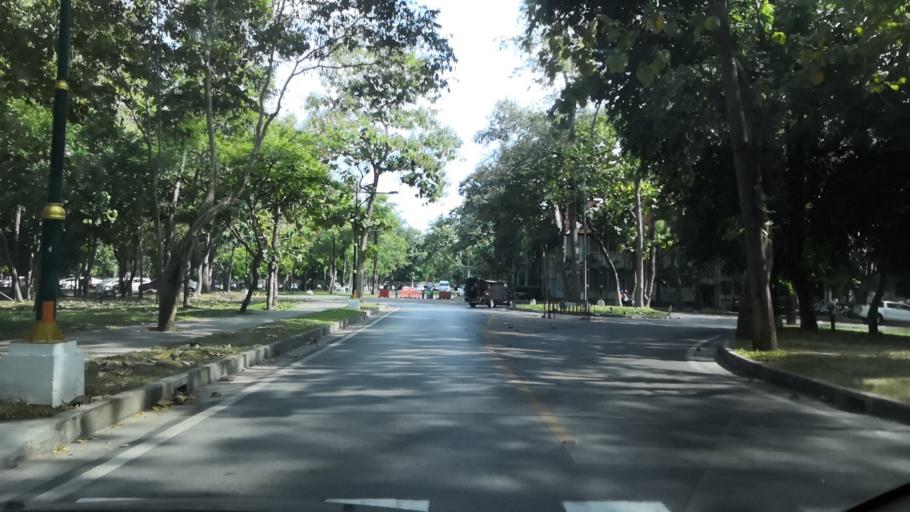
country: TH
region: Chiang Mai
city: Chiang Mai
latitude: 18.8056
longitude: 98.9540
